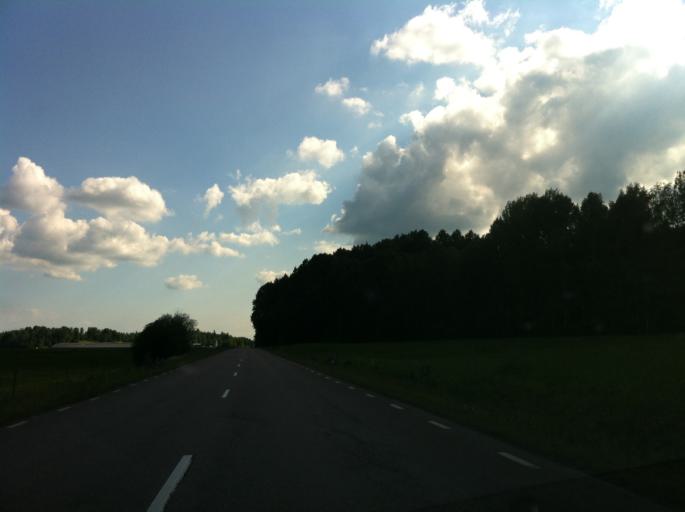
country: SE
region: Vaermland
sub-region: Kils Kommun
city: Kil
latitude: 59.5685
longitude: 13.2926
